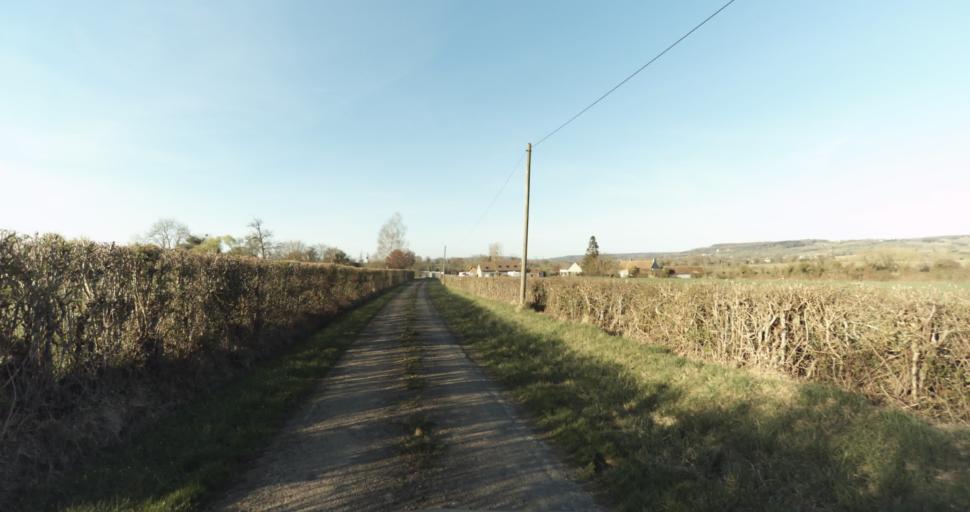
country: FR
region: Lower Normandy
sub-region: Departement de l'Orne
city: Trun
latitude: 48.9130
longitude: 0.0163
